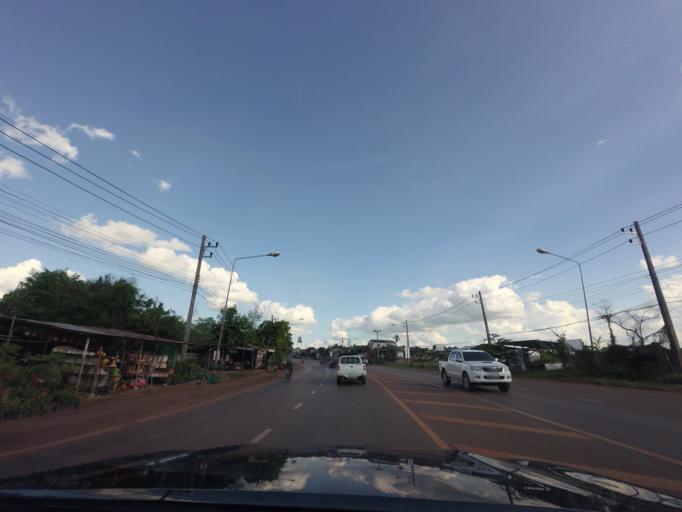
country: TH
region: Changwat Udon Thani
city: Ban Dung
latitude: 17.7053
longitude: 103.2521
